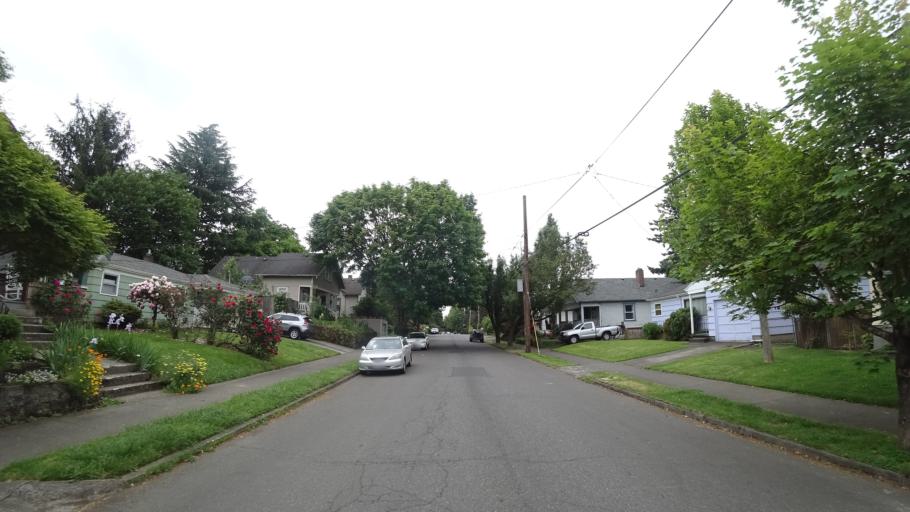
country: US
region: Oregon
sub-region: Clackamas County
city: Milwaukie
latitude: 45.4895
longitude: -122.6344
